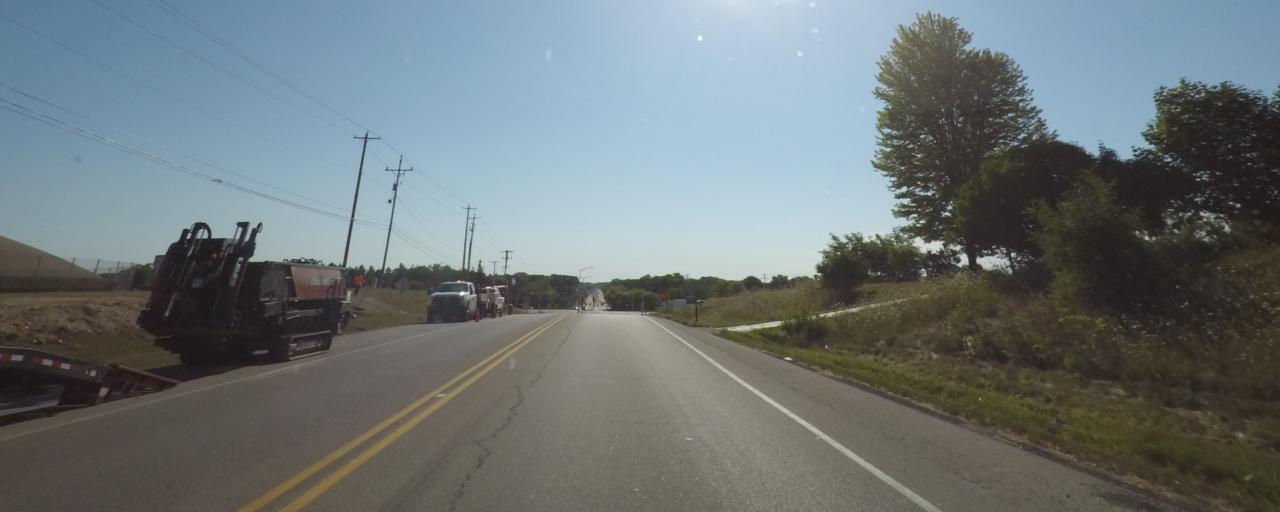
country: US
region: Wisconsin
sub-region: Waukesha County
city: Waukesha
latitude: 42.9885
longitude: -88.2698
